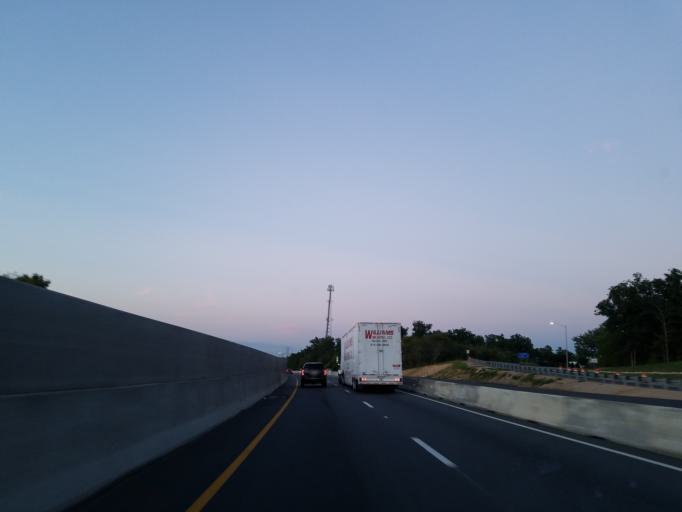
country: US
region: North Carolina
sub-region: Cabarrus County
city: Kannapolis
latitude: 35.4509
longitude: -80.5972
